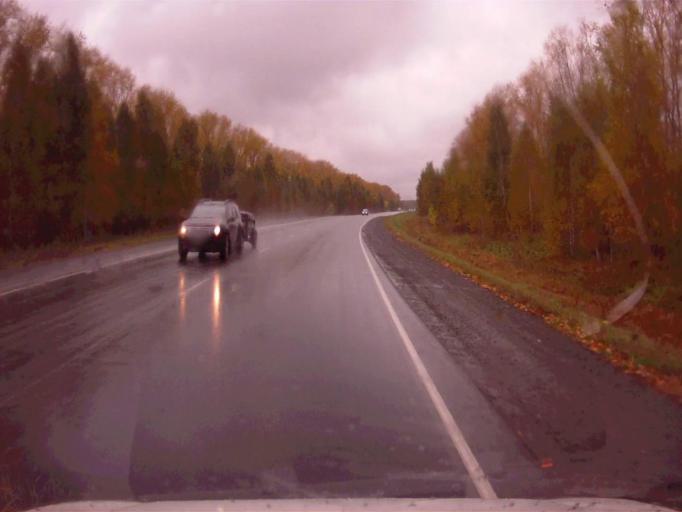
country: RU
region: Chelyabinsk
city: Argayash
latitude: 55.4506
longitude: 60.9375
